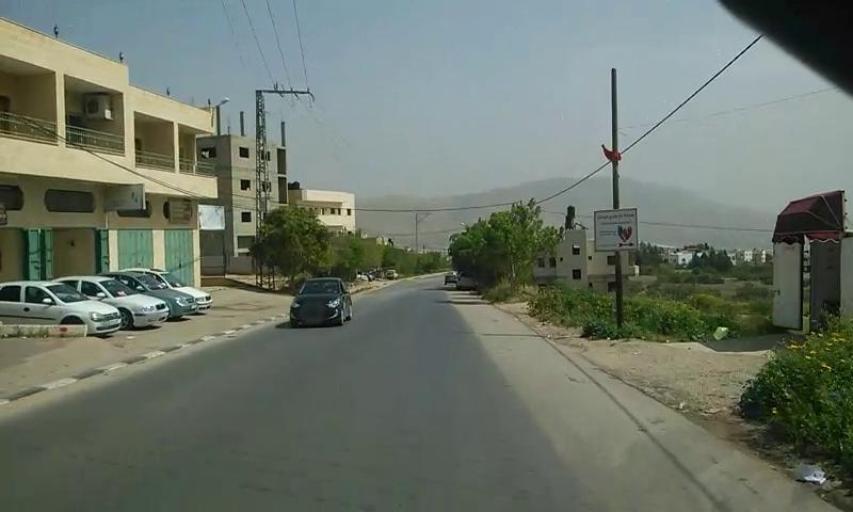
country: PS
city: Al Badhan
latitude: 32.2619
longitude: 35.3305
